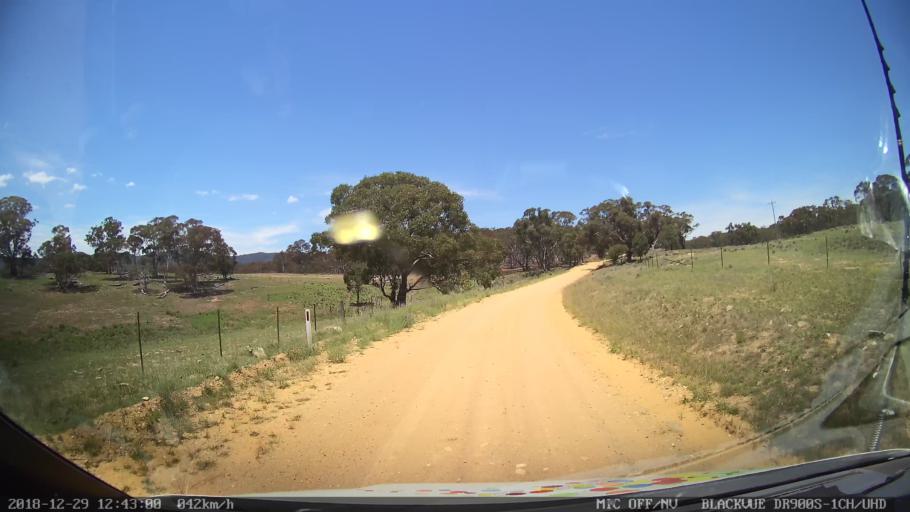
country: AU
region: Australian Capital Territory
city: Macarthur
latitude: -35.6170
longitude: 149.2186
